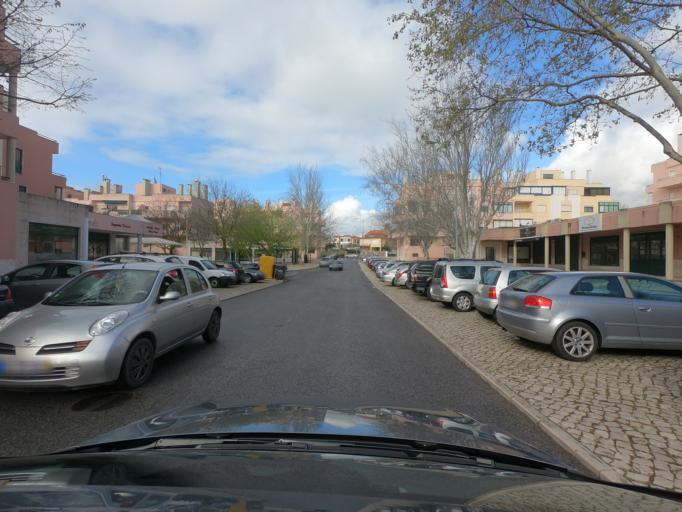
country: PT
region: Lisbon
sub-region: Cascais
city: Sao Domingos de Rana
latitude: 38.7001
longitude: -9.3226
